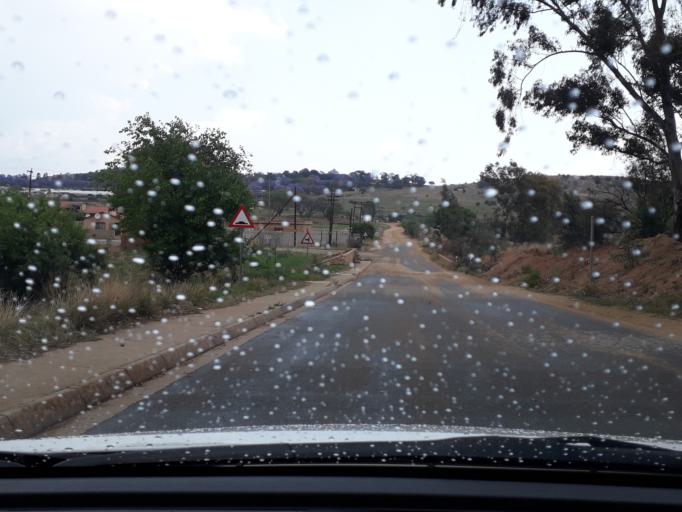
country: ZA
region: Gauteng
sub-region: West Rand District Municipality
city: Muldersdriseloop
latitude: -26.0043
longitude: 27.8531
